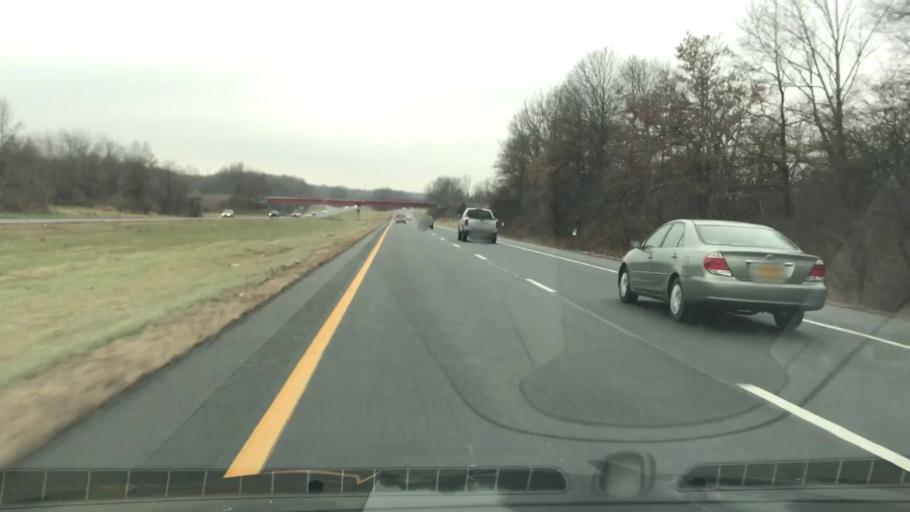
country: US
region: New York
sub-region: Orange County
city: Mechanicstown
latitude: 41.4319
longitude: -74.3878
